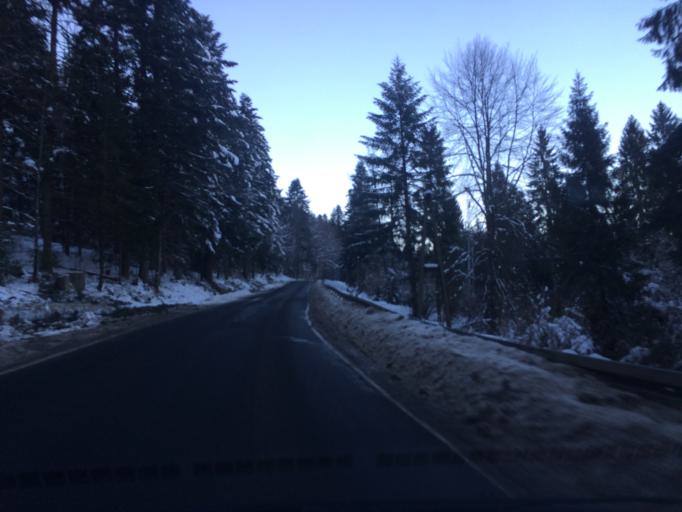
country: PL
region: Subcarpathian Voivodeship
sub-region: Powiat bieszczadzki
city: Lutowiska
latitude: 49.2773
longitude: 22.6847
